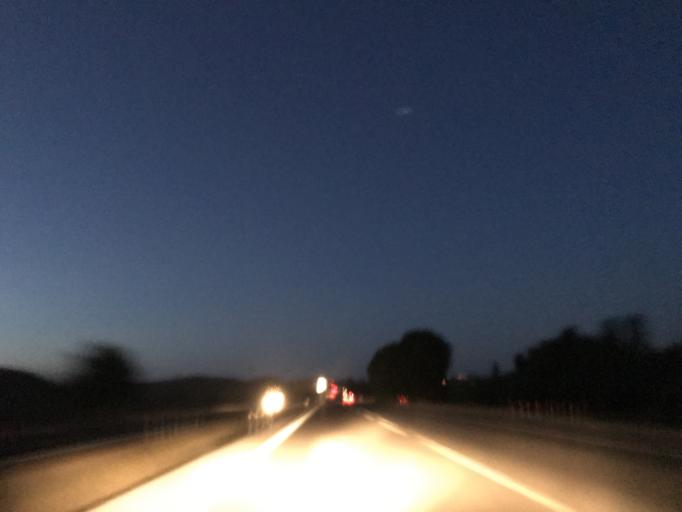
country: TR
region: Yozgat
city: Yerkoy
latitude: 39.6703
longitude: 34.5726
